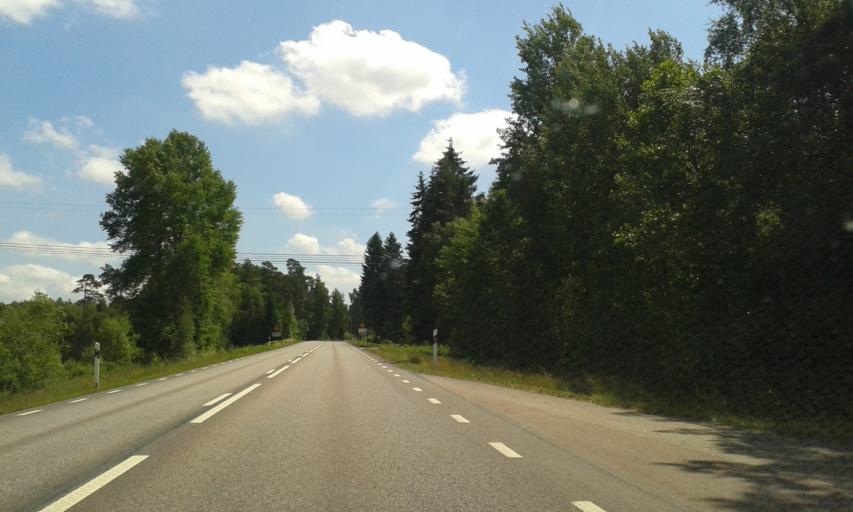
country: SE
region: Kronoberg
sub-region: Vaxjo Kommun
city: Vaexjoe
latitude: 56.8266
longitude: 14.8744
